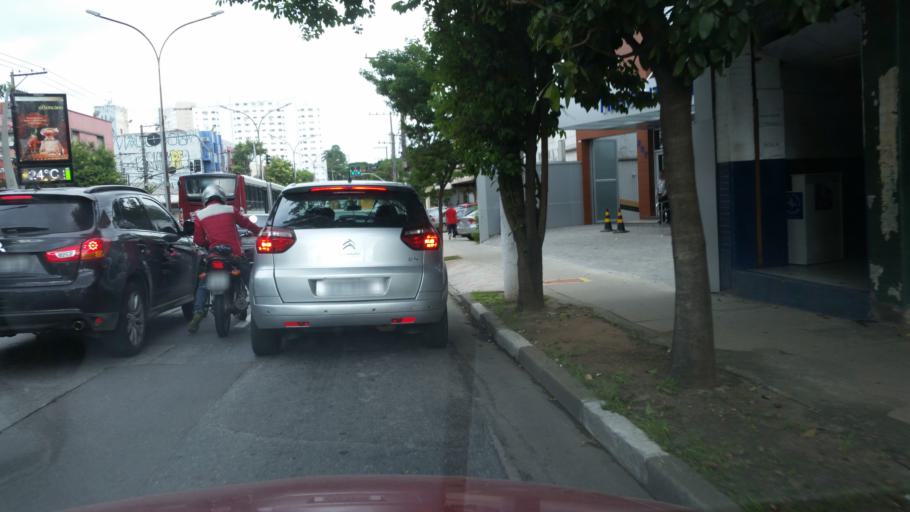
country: BR
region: Sao Paulo
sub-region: Taboao Da Serra
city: Taboao da Serra
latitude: -23.6452
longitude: -46.7036
